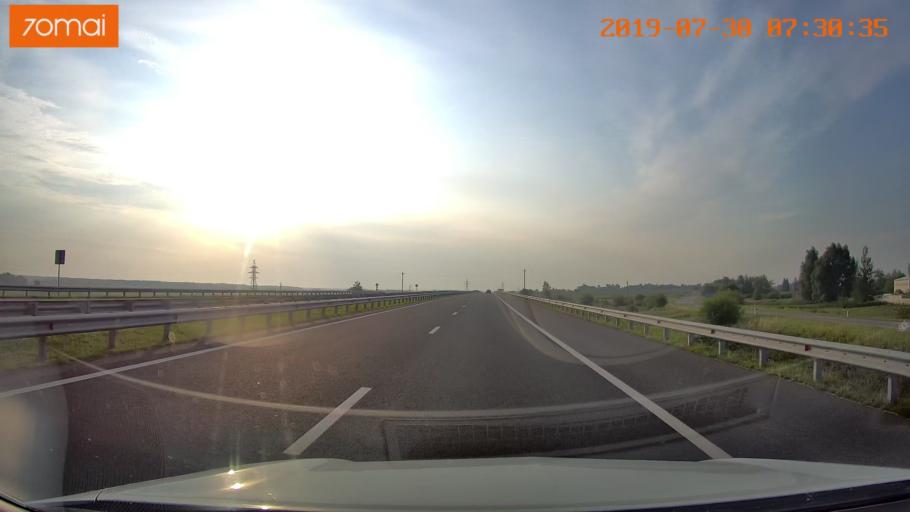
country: RU
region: Kaliningrad
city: Gvardeysk
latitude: 54.6703
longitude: 20.9684
